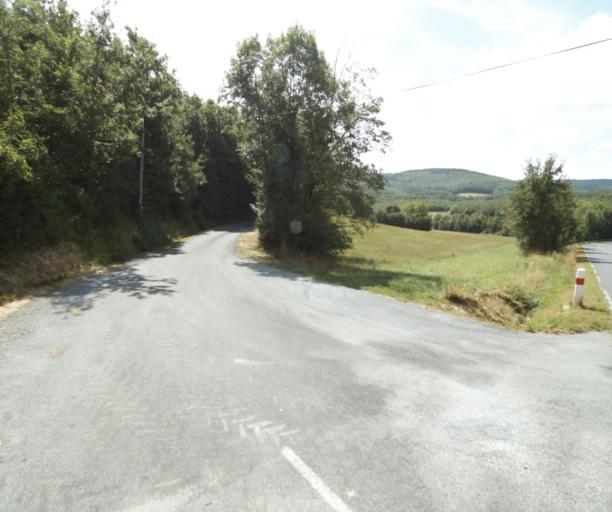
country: FR
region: Midi-Pyrenees
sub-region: Departement du Tarn
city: Dourgne
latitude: 43.4777
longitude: 2.1093
